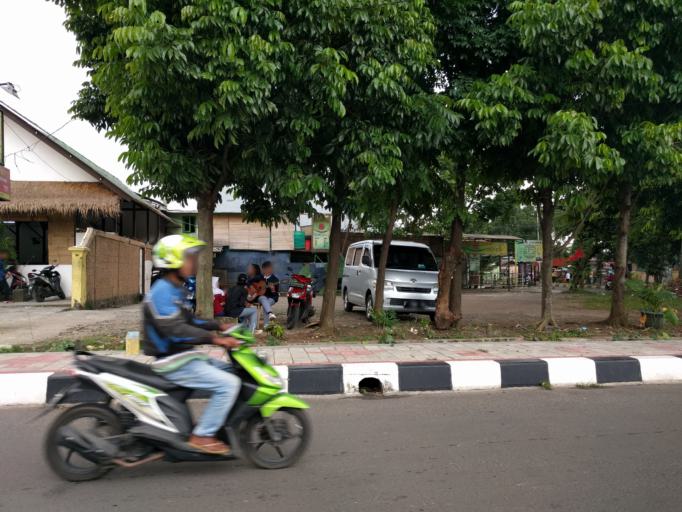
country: ID
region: West Java
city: Bogor
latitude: -6.5818
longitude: 106.8176
